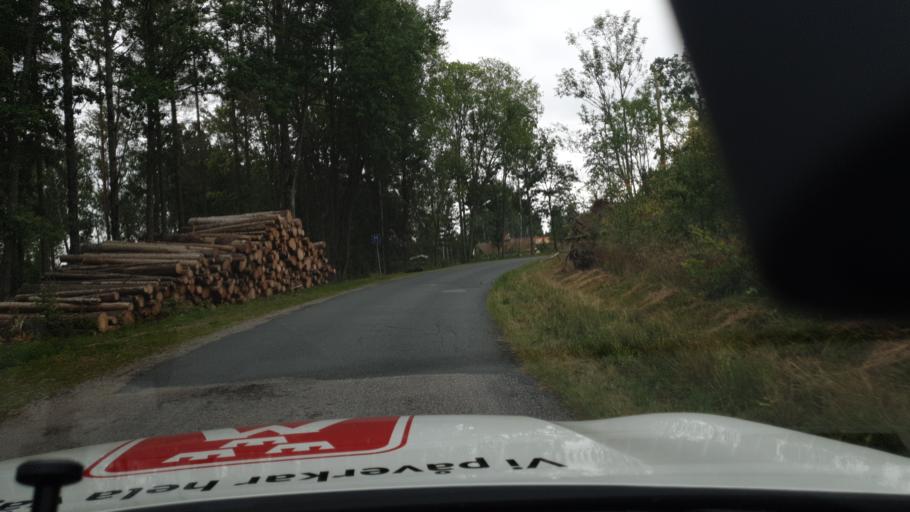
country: SE
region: Soedermanland
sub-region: Strangnas Kommun
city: Akers Styckebruk
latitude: 59.1865
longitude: 17.1360
